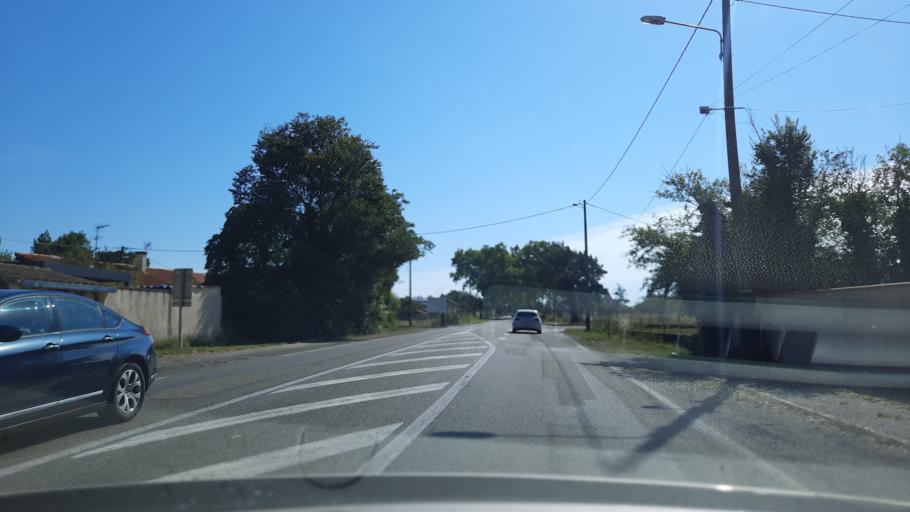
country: FR
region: Midi-Pyrenees
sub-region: Departement du Tarn-et-Garonne
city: Monteils
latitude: 44.1711
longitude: 1.5925
